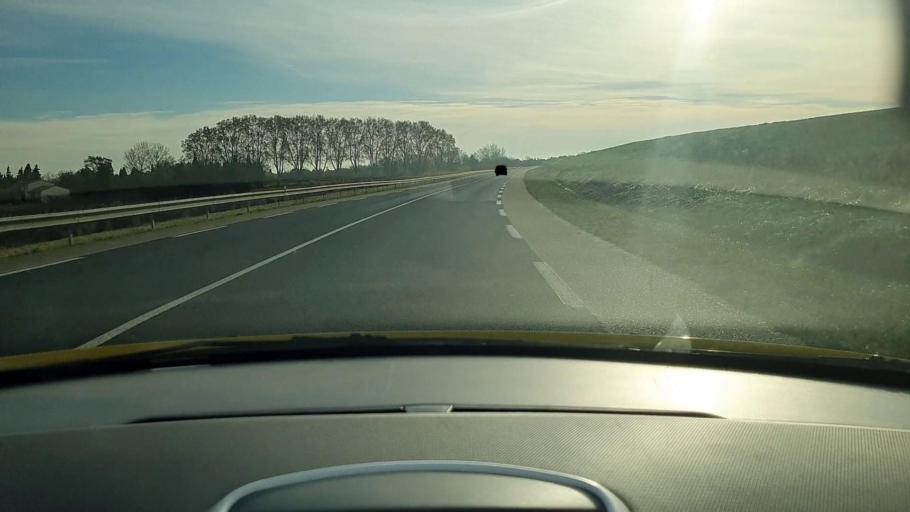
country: FR
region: Languedoc-Roussillon
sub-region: Departement du Gard
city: Fourques
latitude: 43.6986
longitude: 4.5836
